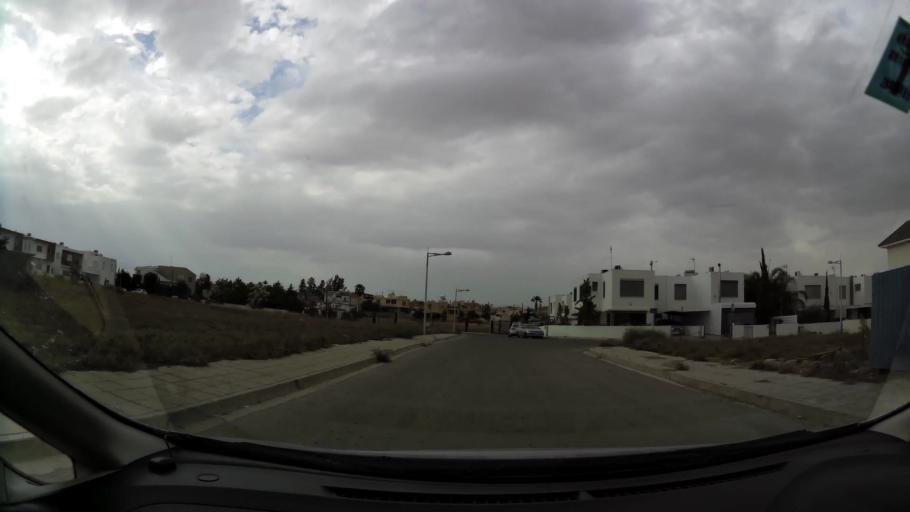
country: CY
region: Lefkosia
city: Geri
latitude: 35.1095
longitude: 33.3914
